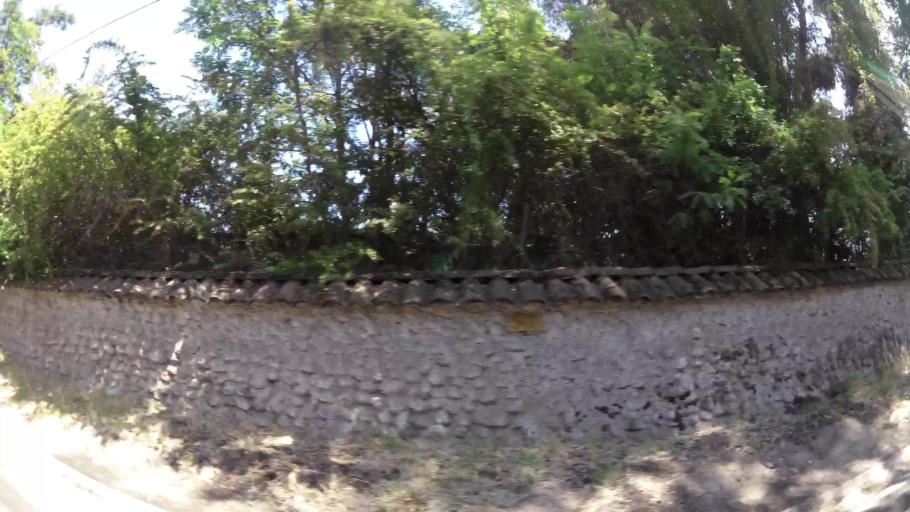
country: CL
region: Santiago Metropolitan
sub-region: Provincia de Maipo
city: San Bernardo
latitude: -33.5732
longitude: -70.7686
